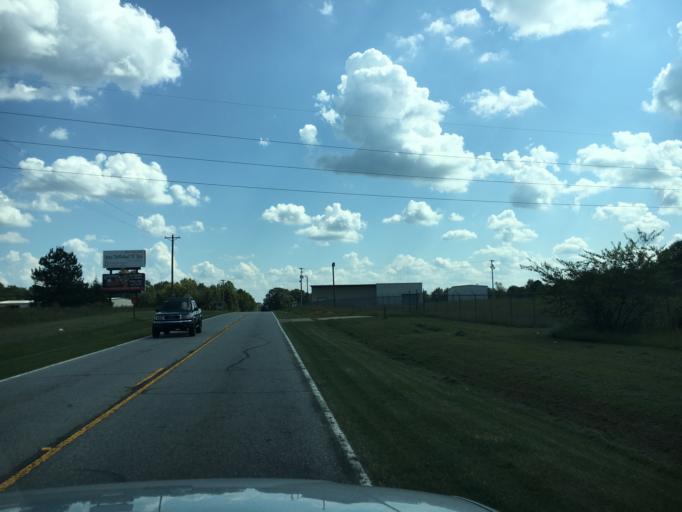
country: US
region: South Carolina
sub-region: Greenville County
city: Fountain Inn
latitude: 34.5969
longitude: -82.1062
